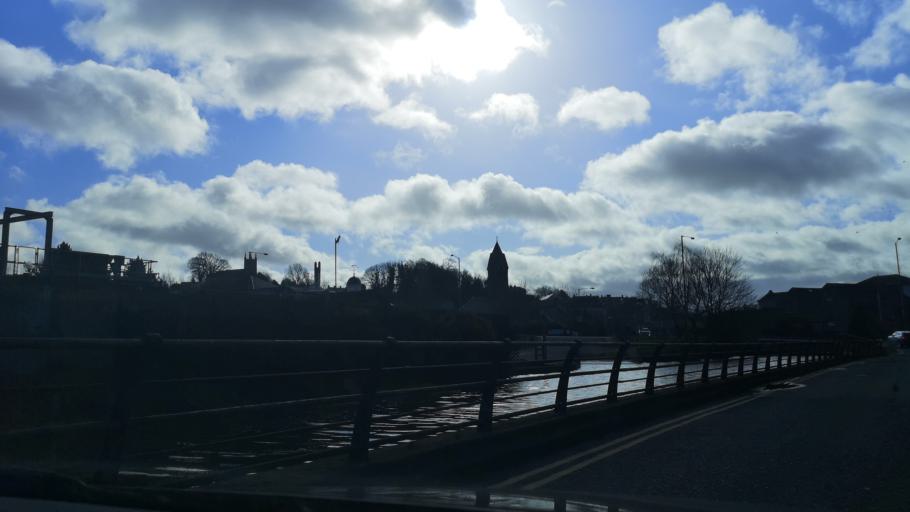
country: GB
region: Northern Ireland
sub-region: Newry and Mourne District
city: Newry
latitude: 54.1805
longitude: -6.3368
